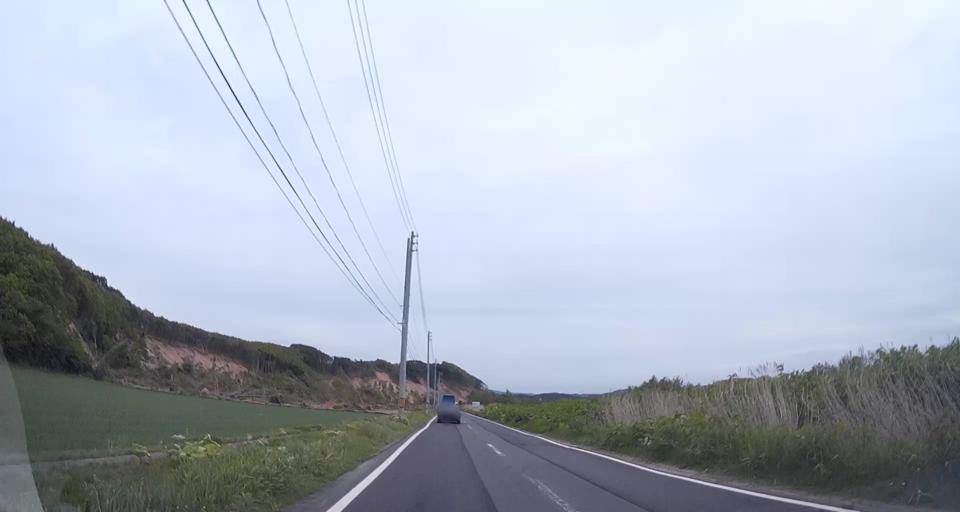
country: JP
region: Hokkaido
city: Chitose
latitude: 42.7433
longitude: 141.9059
